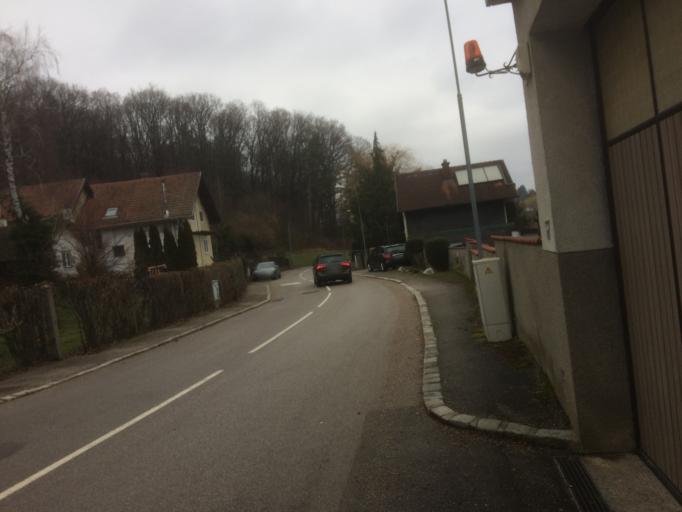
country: AT
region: Lower Austria
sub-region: Politischer Bezirk Wien-Umgebung
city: Gablitz
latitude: 48.2232
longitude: 16.1344
